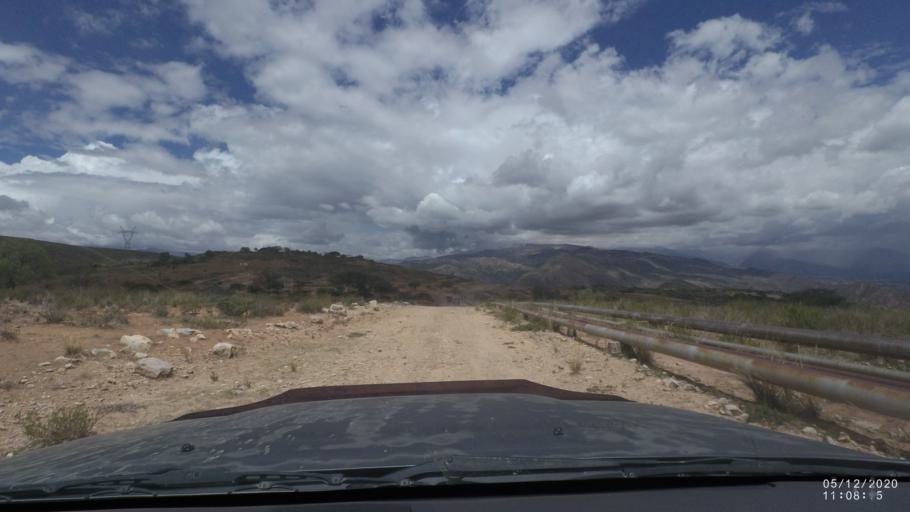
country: BO
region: Cochabamba
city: Sipe Sipe
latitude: -17.5516
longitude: -66.3128
